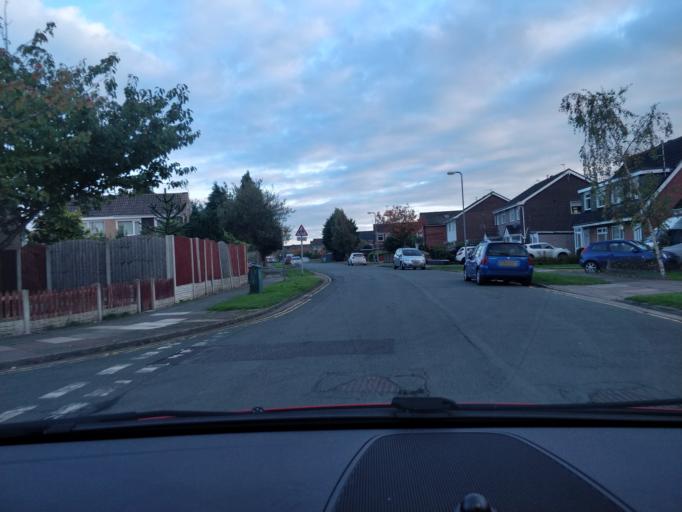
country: GB
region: England
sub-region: Sefton
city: Southport
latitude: 53.6319
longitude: -2.9757
